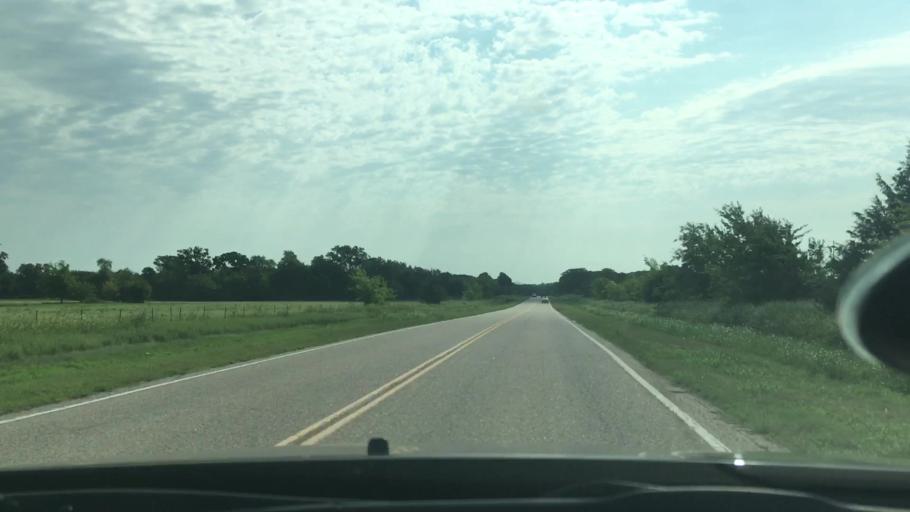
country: US
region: Oklahoma
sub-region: Bryan County
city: Durant
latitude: 34.0857
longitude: -96.3941
